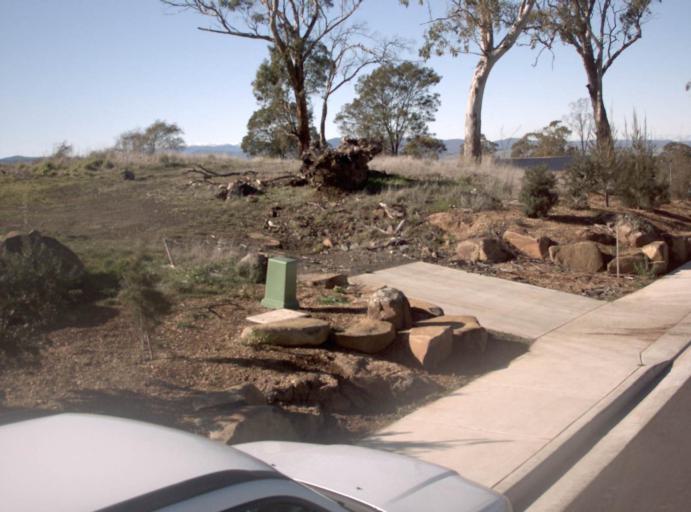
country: AU
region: Tasmania
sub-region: Launceston
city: Summerhill
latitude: -41.4727
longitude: 147.1500
